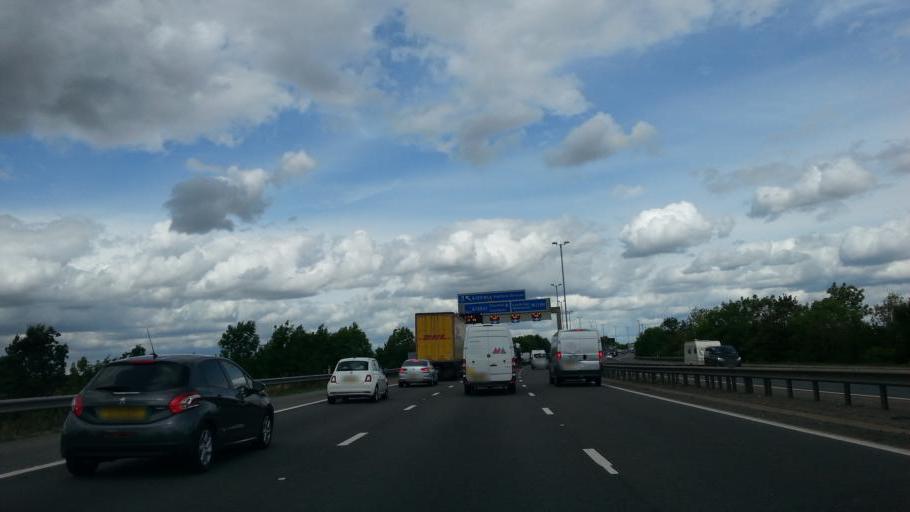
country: GB
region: England
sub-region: Essex
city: Little Hallingbury
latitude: 51.8545
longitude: 0.1850
